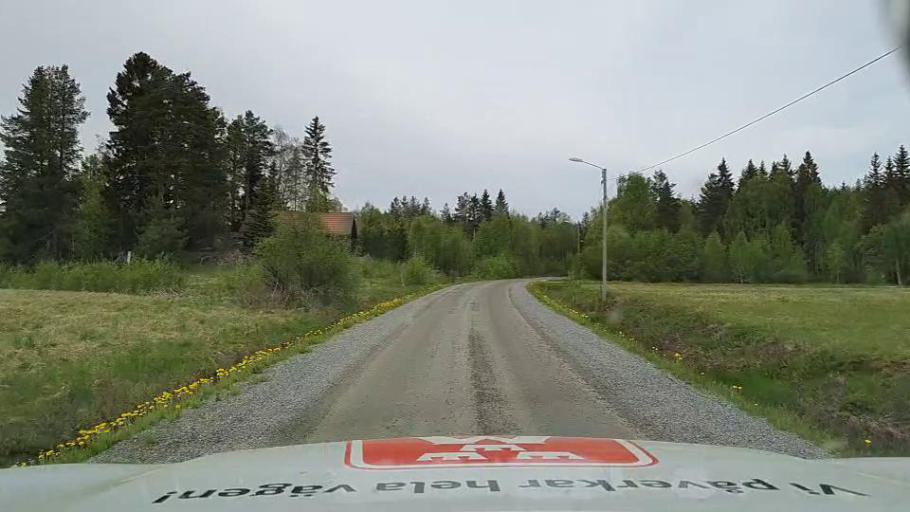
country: SE
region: Jaemtland
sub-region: Braecke Kommun
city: Braecke
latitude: 62.4543
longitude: 14.9152
